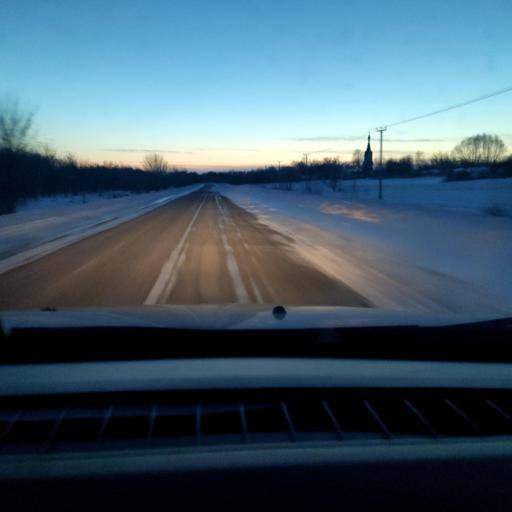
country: RU
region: Samara
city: Georgiyevka
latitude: 53.3212
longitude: 50.8673
